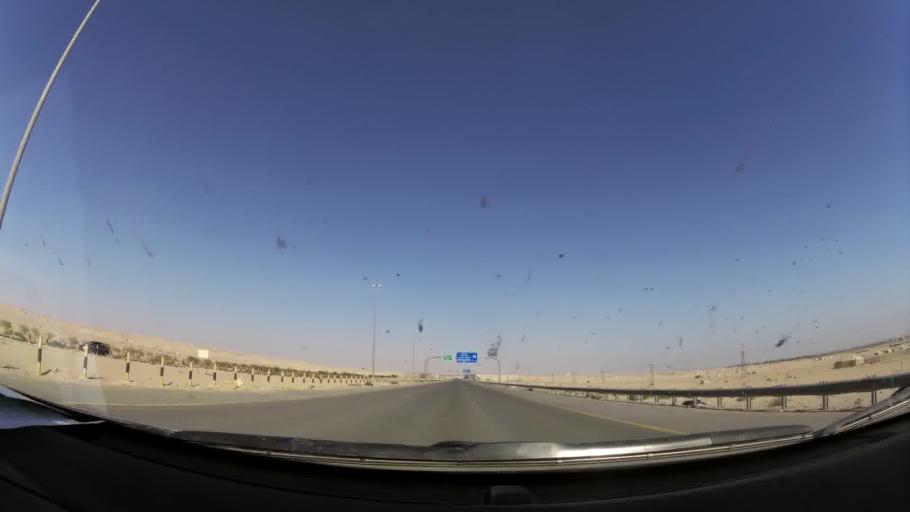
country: KW
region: Muhafazat al Jahra'
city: Al Jahra'
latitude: 29.4012
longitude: 47.6907
